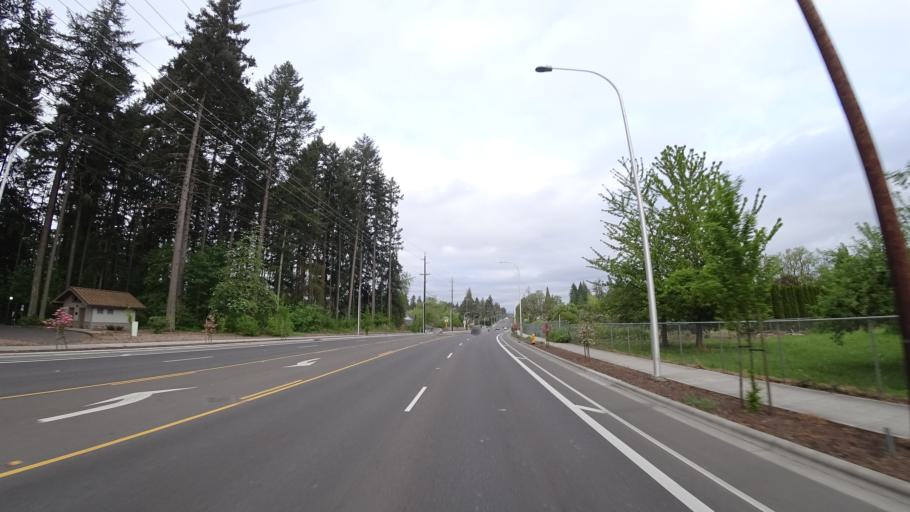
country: US
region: Oregon
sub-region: Washington County
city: Rockcreek
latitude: 45.5201
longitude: -122.9185
